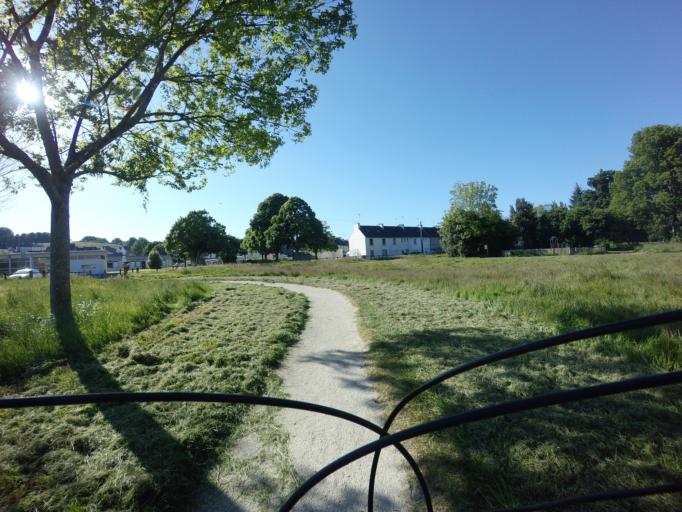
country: FR
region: Brittany
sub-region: Departement du Finistere
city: Quimper
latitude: 48.0067
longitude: -4.1156
